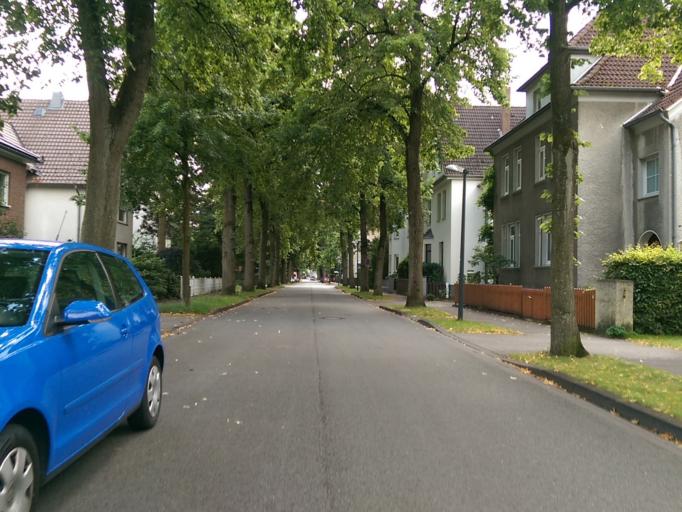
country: DE
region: North Rhine-Westphalia
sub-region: Regierungsbezirk Detmold
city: Guetersloh
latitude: 51.9137
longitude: 8.3752
